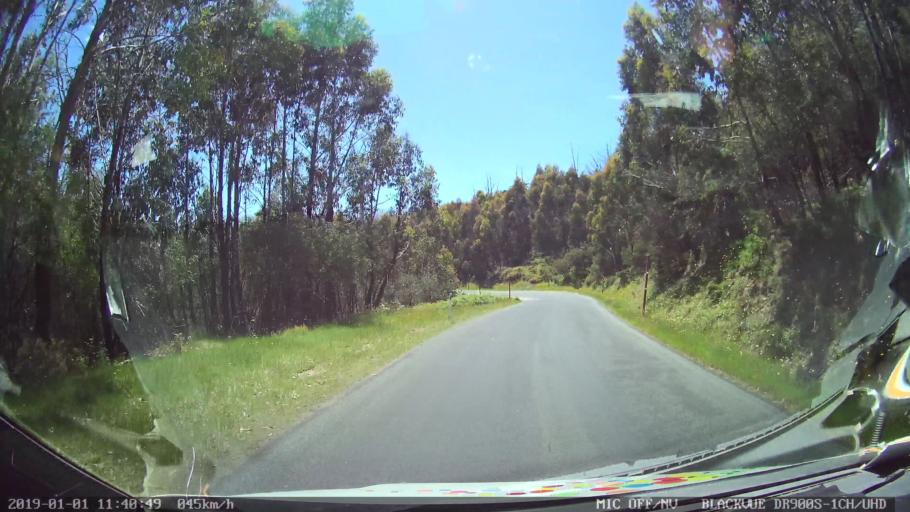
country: AU
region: New South Wales
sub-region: Snowy River
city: Jindabyne
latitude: -35.9176
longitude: 148.3882
